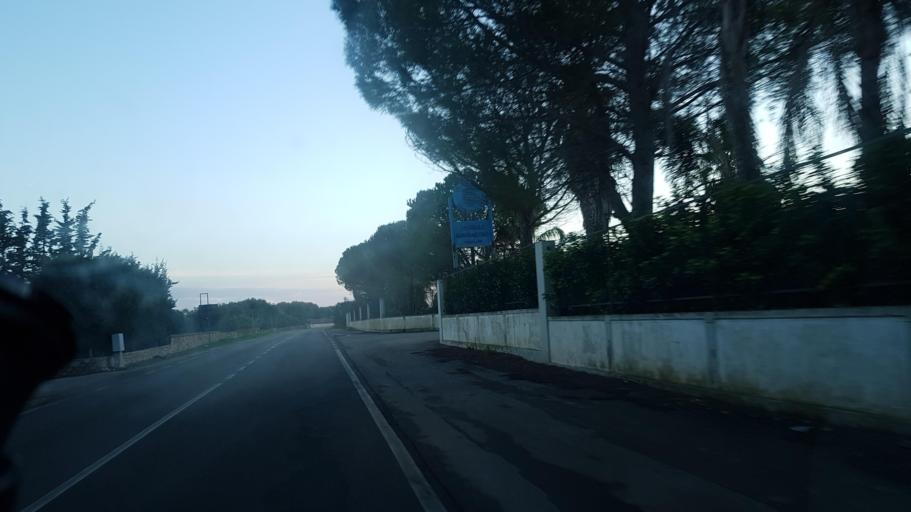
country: IT
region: Apulia
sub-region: Provincia di Brindisi
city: San Michele Salentino
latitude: 40.6065
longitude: 17.6527
